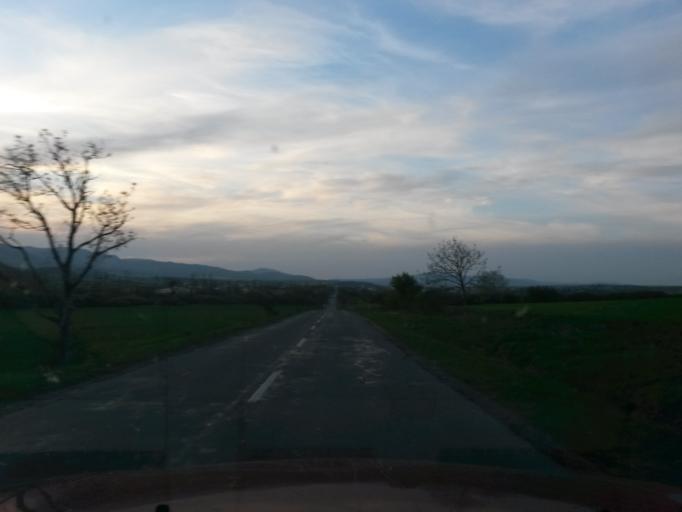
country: HU
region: Borsod-Abauj-Zemplen
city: Satoraljaujhely
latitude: 48.4980
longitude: 21.6310
